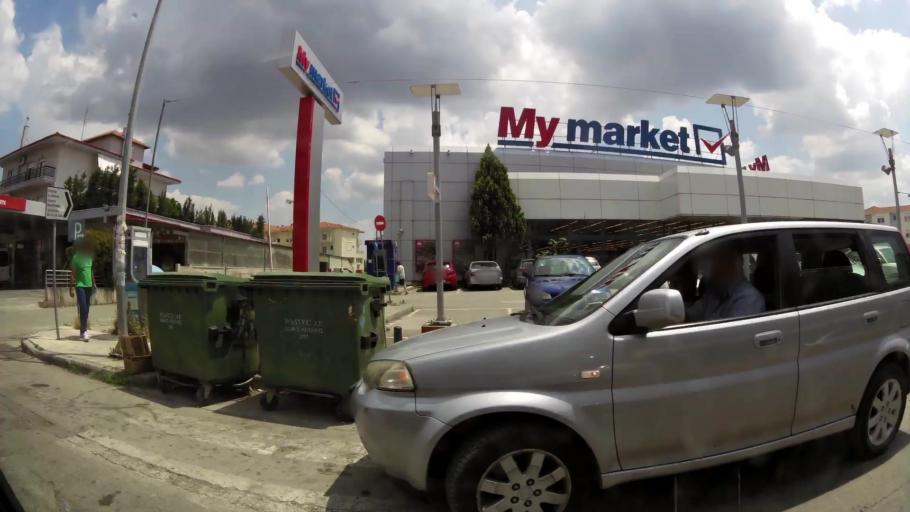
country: GR
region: West Macedonia
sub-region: Nomos Kozanis
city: Kozani
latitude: 40.2993
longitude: 21.7983
